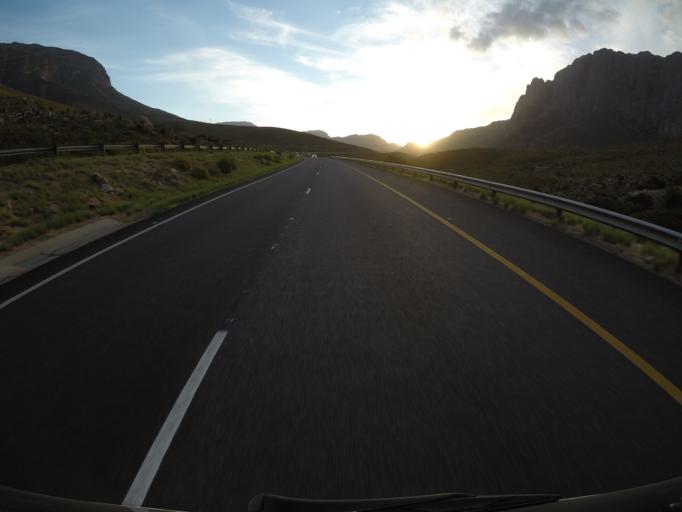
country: ZA
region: Western Cape
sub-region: Cape Winelands District Municipality
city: Paarl
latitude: -33.7239
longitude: 19.1715
